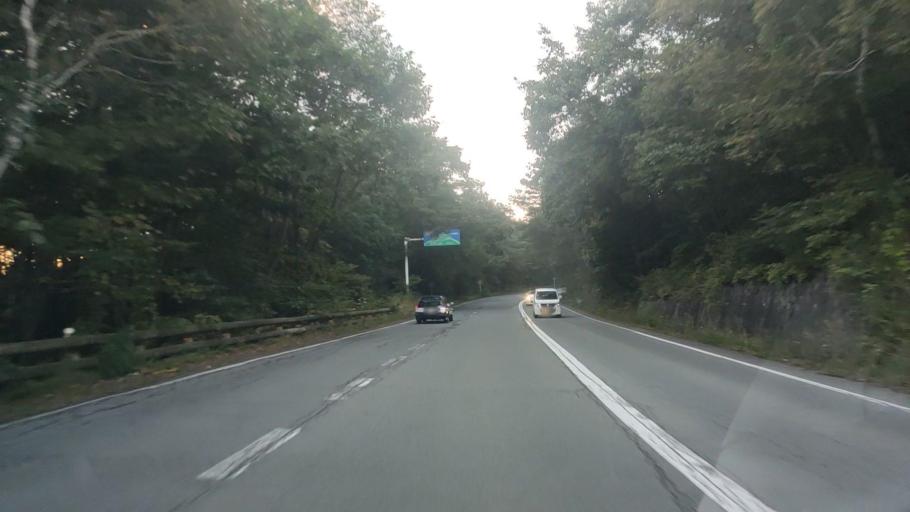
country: JP
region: Nagano
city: Komoro
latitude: 36.3884
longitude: 138.5859
